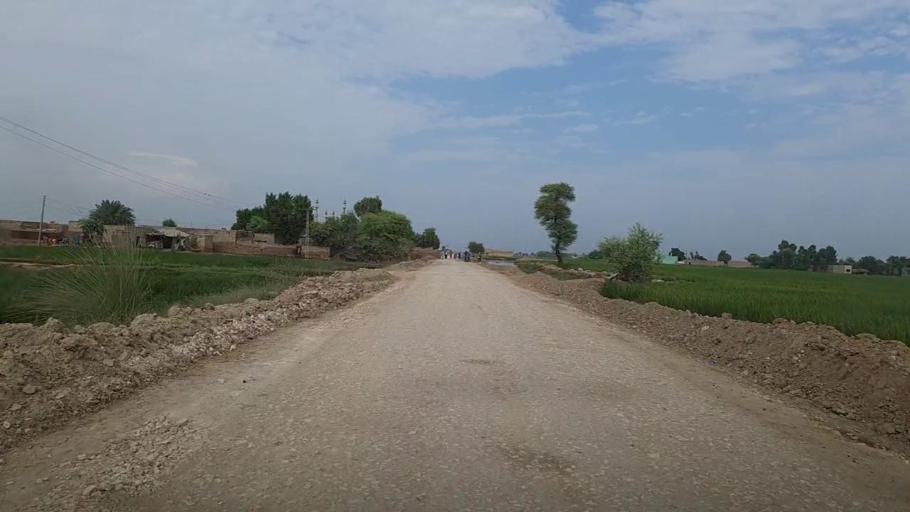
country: PK
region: Sindh
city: Thul
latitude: 28.2539
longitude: 68.8029
